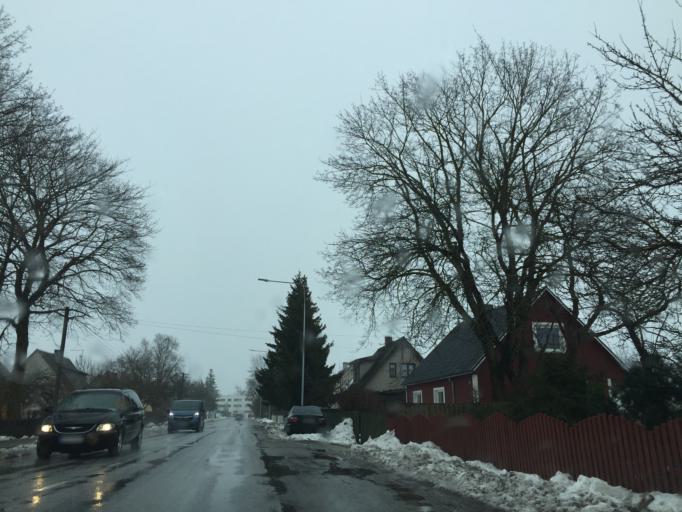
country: EE
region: Saare
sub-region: Kuressaare linn
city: Kuressaare
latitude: 58.2597
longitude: 22.4951
